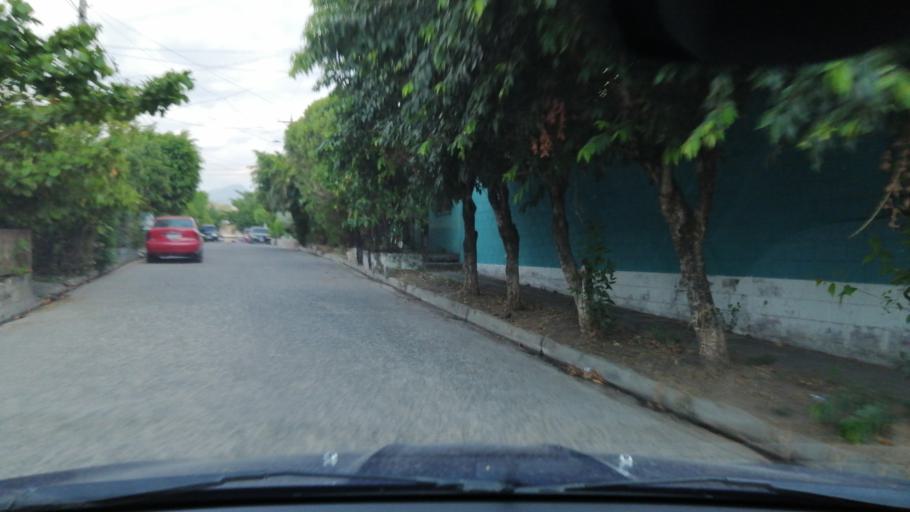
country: SV
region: Santa Ana
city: Metapan
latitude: 14.3297
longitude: -89.4385
